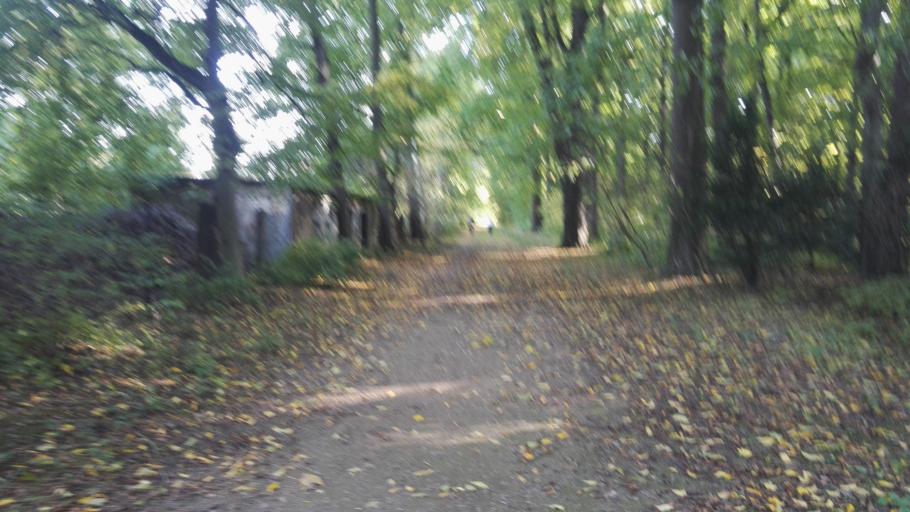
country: DE
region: Saxony
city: Dresden
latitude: 51.0408
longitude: 13.7587
